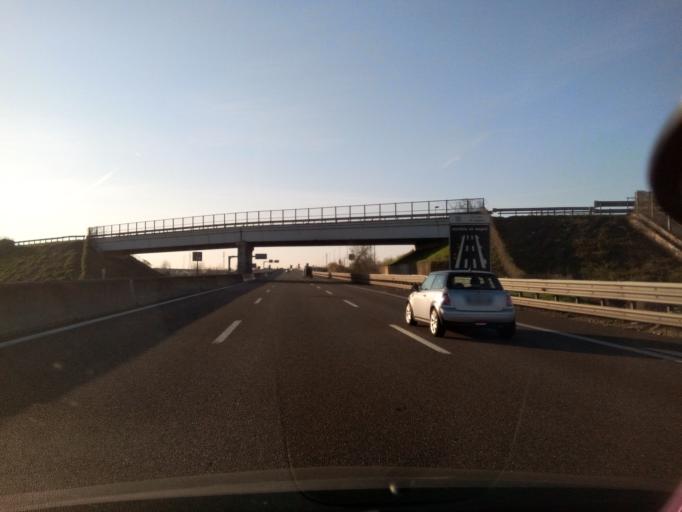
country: IT
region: Emilia-Romagna
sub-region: Provincia di Piacenza
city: Pontenure
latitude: 45.0396
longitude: 9.7598
